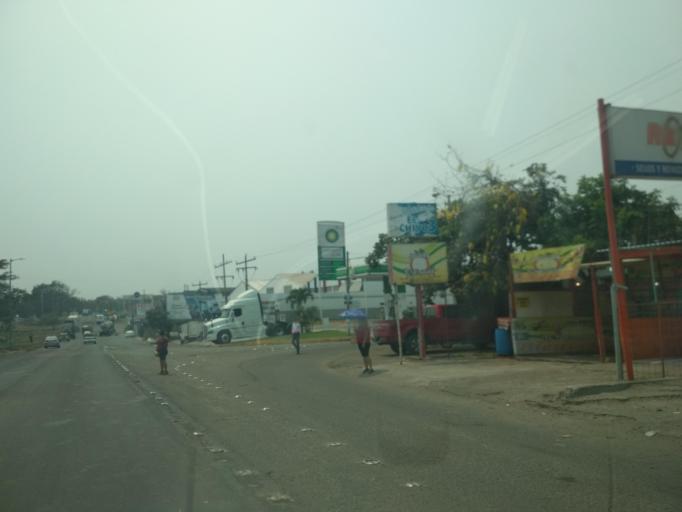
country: MX
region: Veracruz
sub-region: Veracruz
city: Lomas de Rio Medio Cuatro
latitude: 19.1695
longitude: -96.2258
